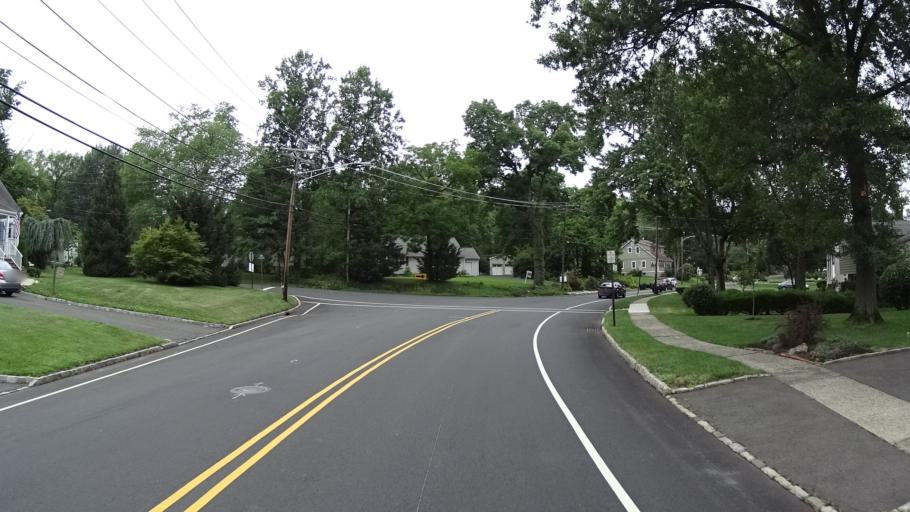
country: US
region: New Jersey
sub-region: Union County
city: New Providence
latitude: 40.6894
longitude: -74.4187
